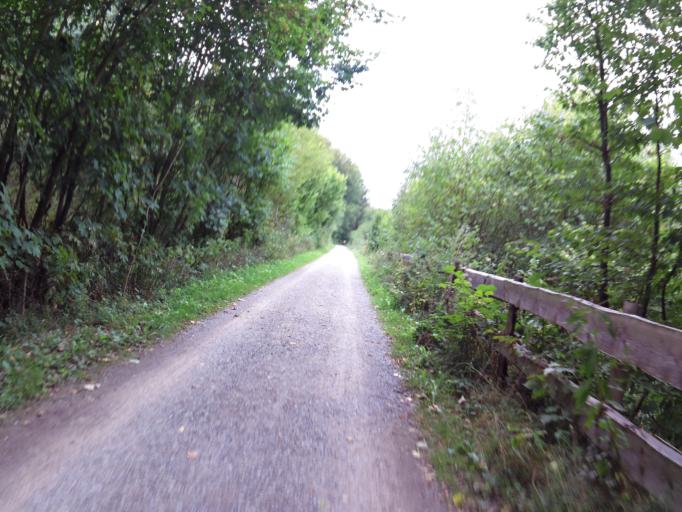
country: DE
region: North Rhine-Westphalia
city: Heimbach
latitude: 50.6346
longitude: 6.4324
